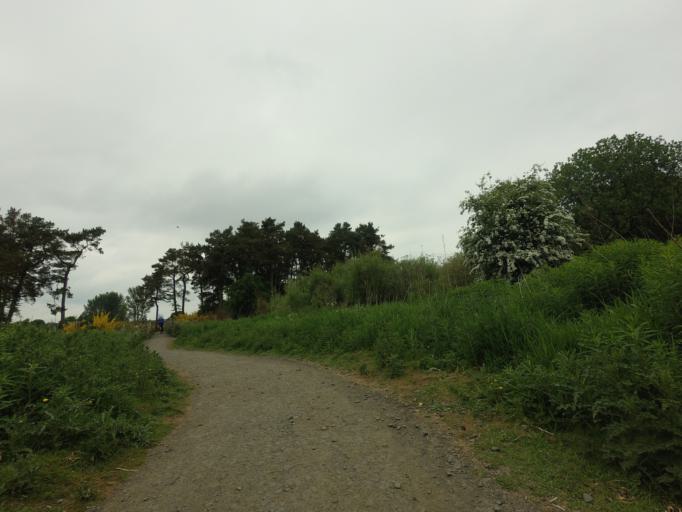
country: GB
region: Scotland
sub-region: Perth and Kinross
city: Kinross
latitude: 56.1986
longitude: -3.4171
